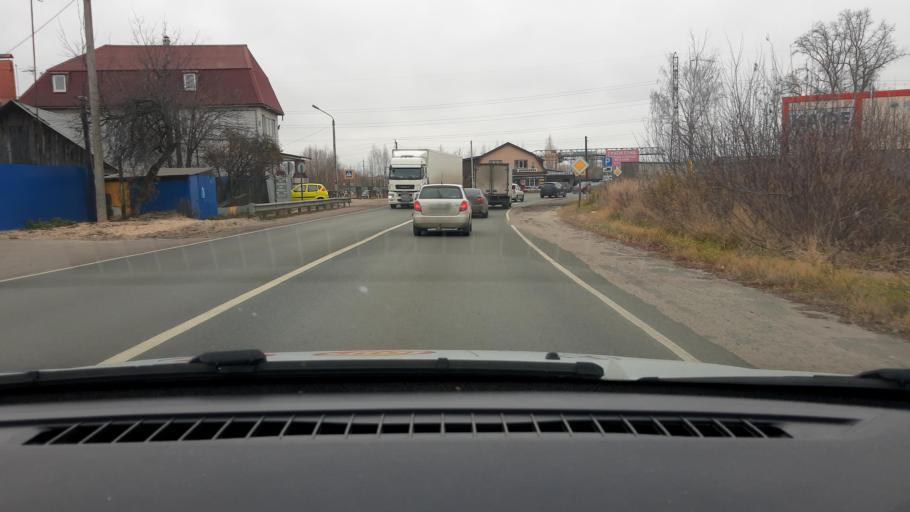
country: RU
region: Nizjnij Novgorod
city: Novaya Balakhna
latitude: 56.5005
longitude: 43.5944
